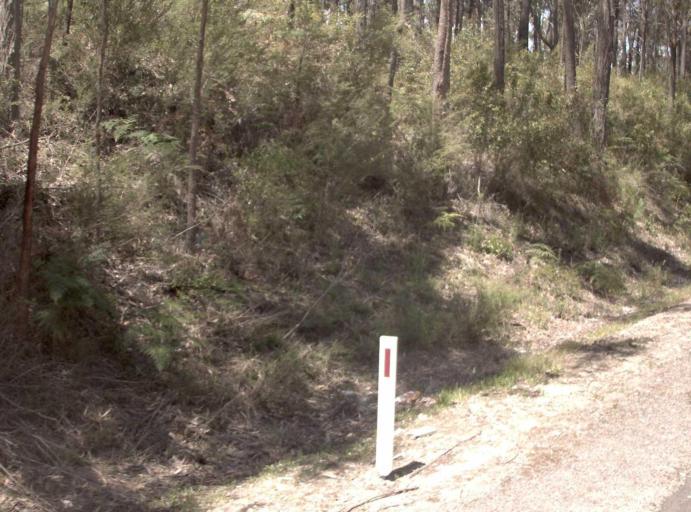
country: AU
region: Victoria
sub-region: East Gippsland
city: Lakes Entrance
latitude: -37.7029
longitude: 148.6444
